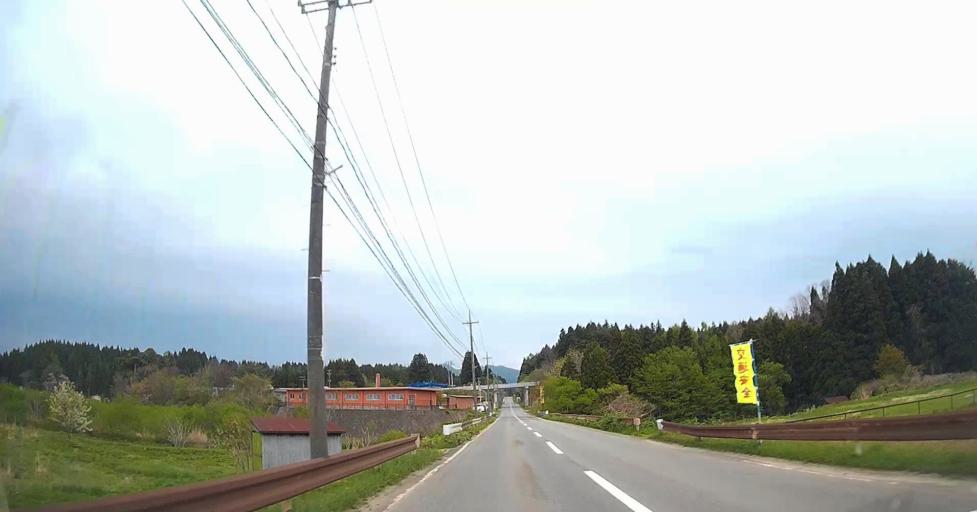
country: JP
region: Aomori
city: Goshogawara
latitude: 41.1779
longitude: 140.4776
